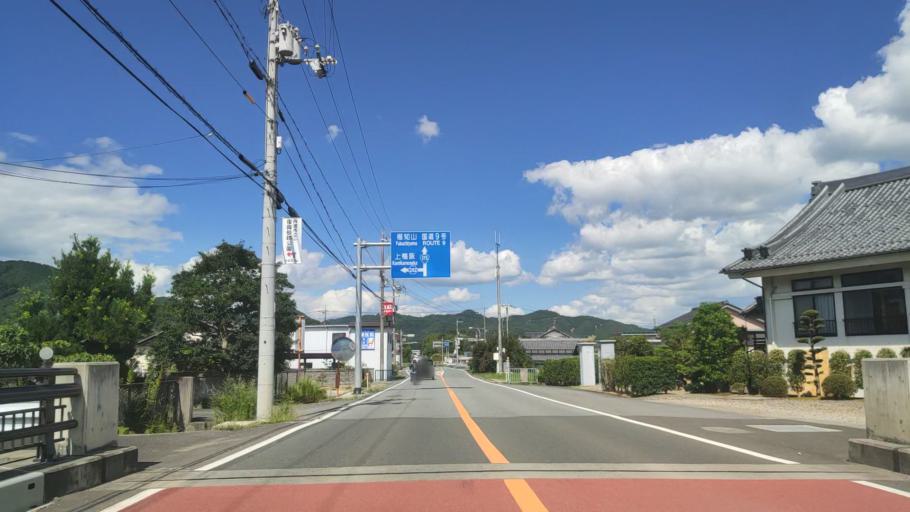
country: JP
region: Kyoto
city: Fukuchiyama
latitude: 35.2261
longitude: 135.1296
